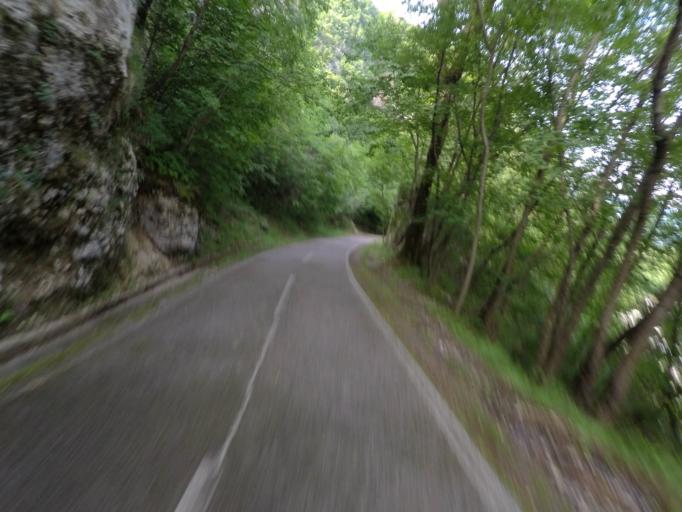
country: IT
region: Friuli Venezia Giulia
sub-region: Provincia di Udine
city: Amaro
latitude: 46.3610
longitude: 13.1021
